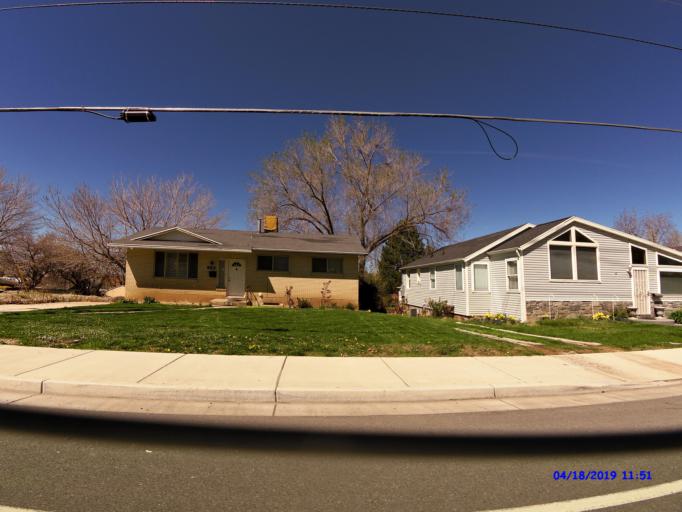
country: US
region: Utah
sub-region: Weber County
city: Ogden
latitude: 41.2522
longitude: -111.9480
